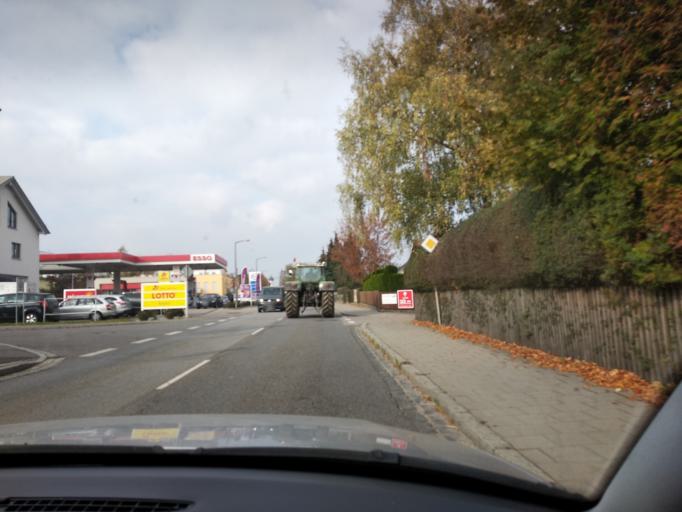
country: DE
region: Bavaria
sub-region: Upper Bavaria
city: Markt Schwaben
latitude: 48.1847
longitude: 11.8694
